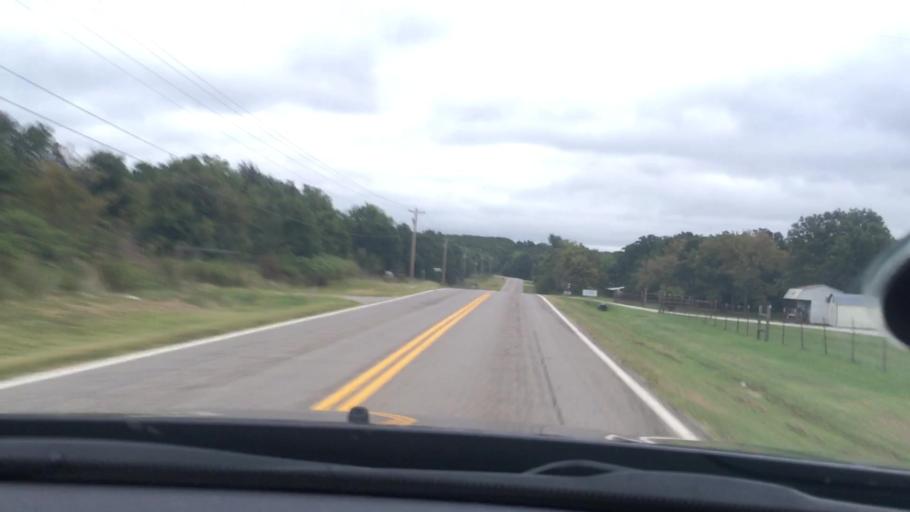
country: US
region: Oklahoma
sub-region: Sequoyah County
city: Vian
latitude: 35.6025
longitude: -95.0104
